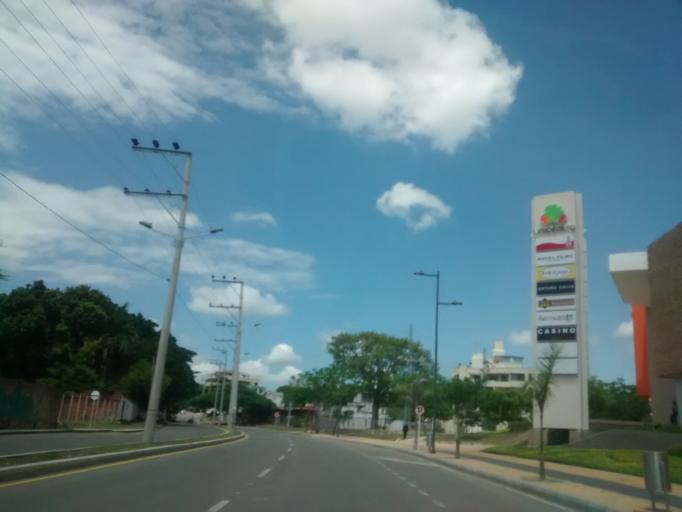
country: CO
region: Cundinamarca
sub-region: Girardot
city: Girardot City
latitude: 4.3073
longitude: -74.7971
